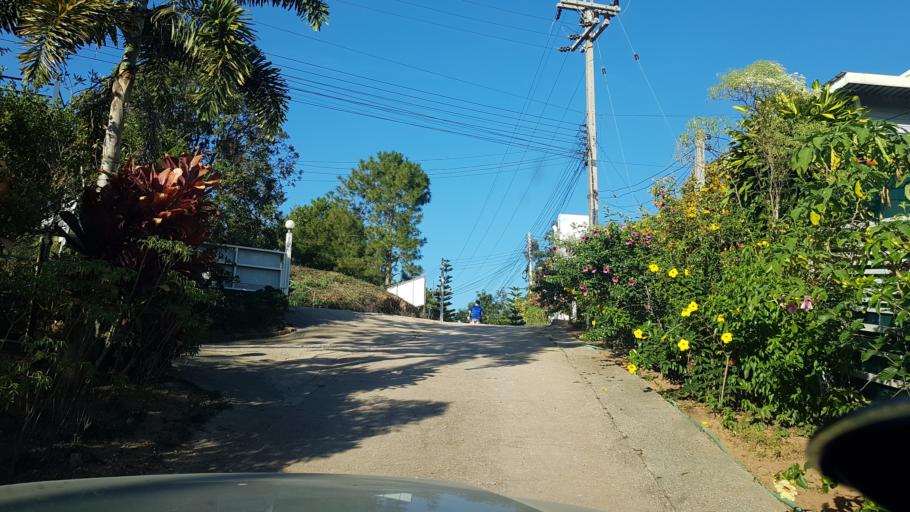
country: TH
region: Phetchabun
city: Khao Kho
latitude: 16.6456
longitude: 100.9999
